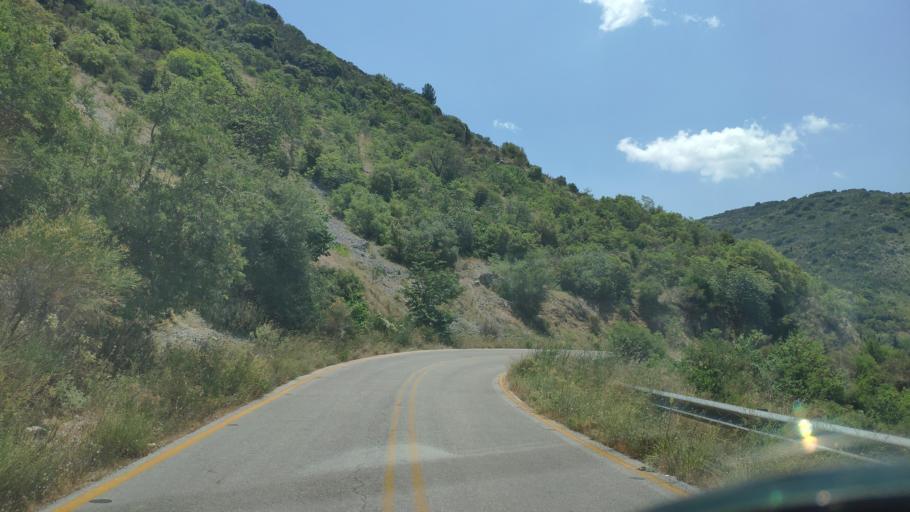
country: GR
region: Ionian Islands
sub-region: Lefkada
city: Nidri
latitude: 38.7499
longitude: 20.6206
